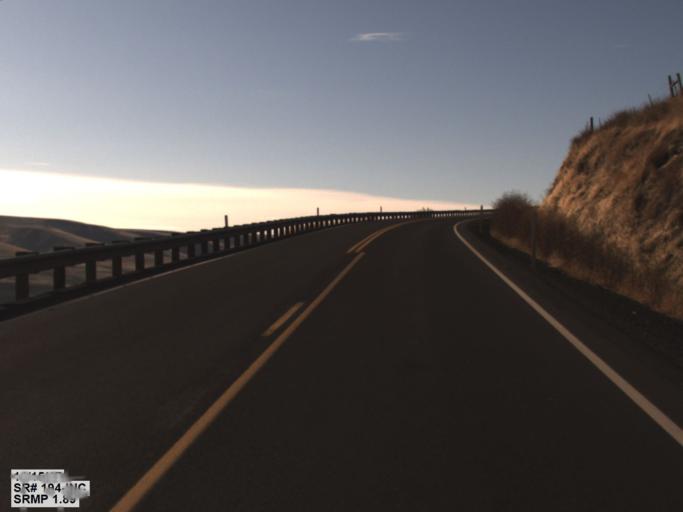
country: US
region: Washington
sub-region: Whitman County
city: Colfax
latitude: 46.7141
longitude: -117.4697
